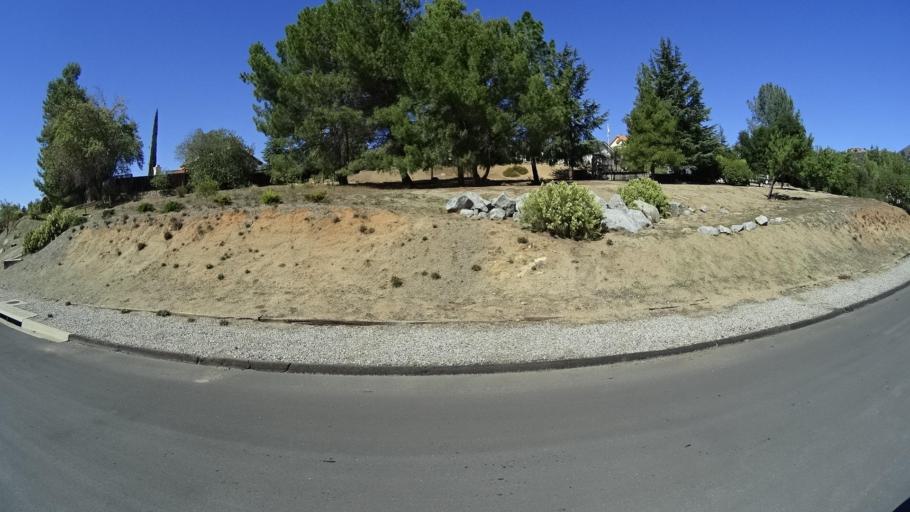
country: US
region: California
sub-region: San Diego County
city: Alpine
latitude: 32.8396
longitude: -116.7607
